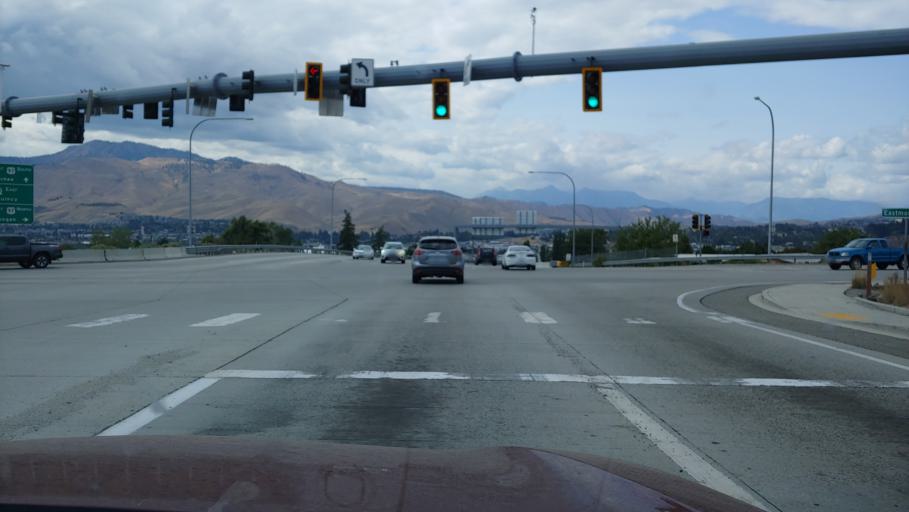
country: US
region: Washington
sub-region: Chelan County
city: Sunnyslope
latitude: 47.4679
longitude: -120.2990
